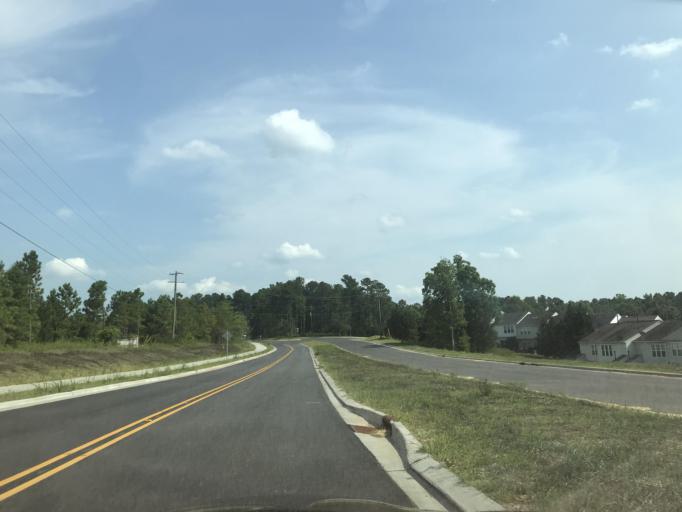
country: US
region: North Carolina
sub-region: Wake County
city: Morrisville
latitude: 35.8408
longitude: -78.8736
